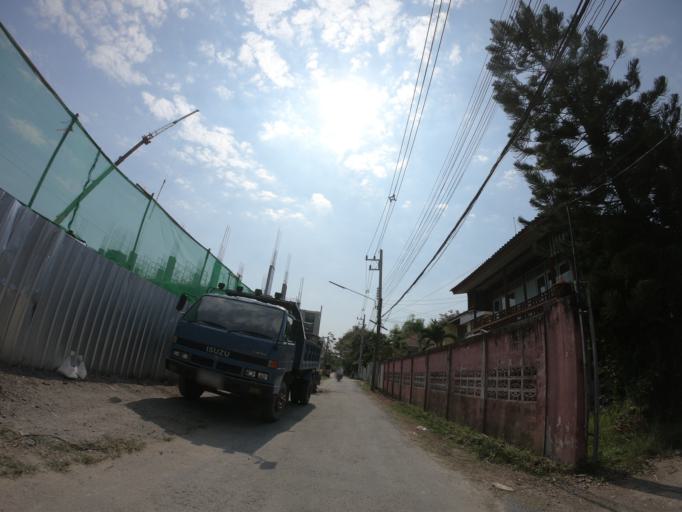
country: TH
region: Chiang Mai
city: Chiang Mai
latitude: 18.7846
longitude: 98.9675
